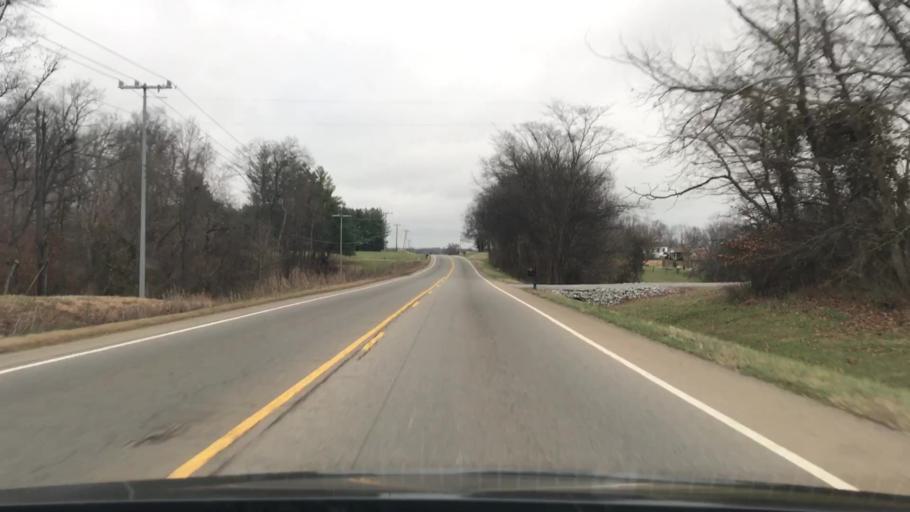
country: US
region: Kentucky
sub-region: Todd County
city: Guthrie
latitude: 36.6148
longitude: -87.2426
